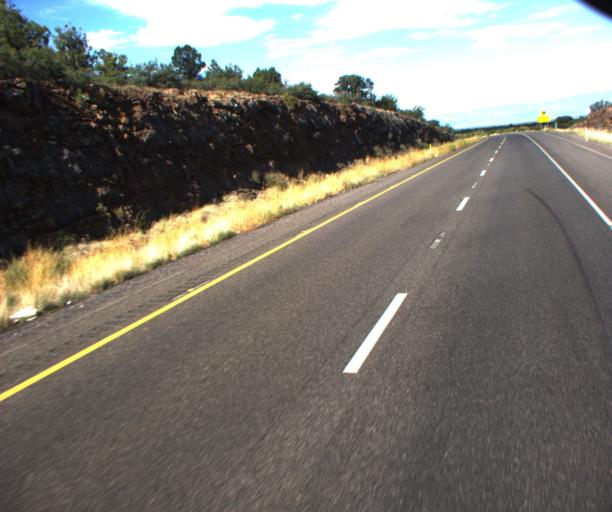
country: US
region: Arizona
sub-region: Yavapai County
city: Village of Oak Creek (Big Park)
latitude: 34.7777
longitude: -111.6308
